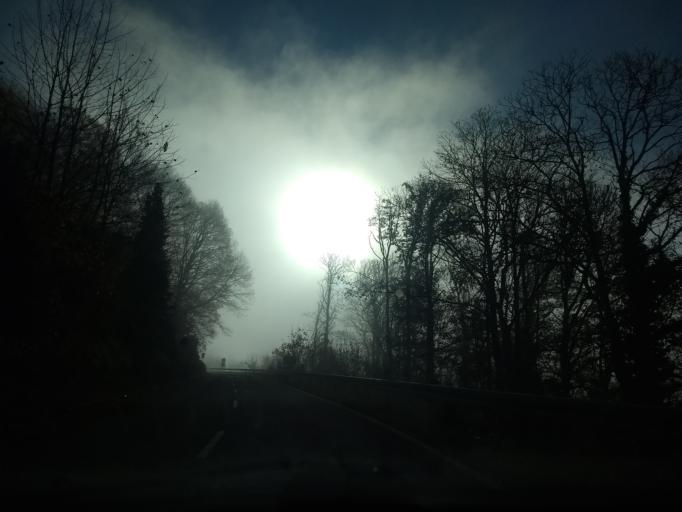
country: DE
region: Baden-Wuerttemberg
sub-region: Karlsruhe Region
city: Baden-Baden
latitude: 48.7848
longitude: 8.2682
